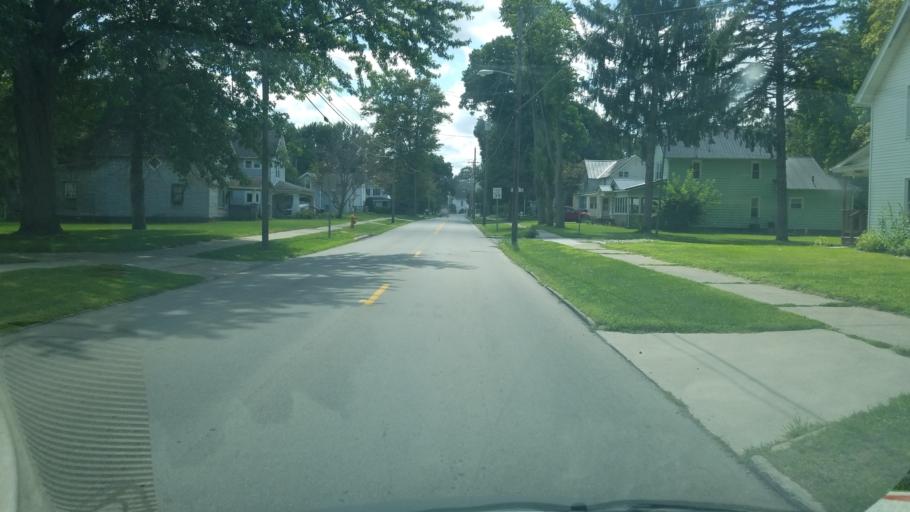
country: US
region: Ohio
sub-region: Henry County
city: Liberty Center
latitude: 41.4480
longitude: -84.0088
